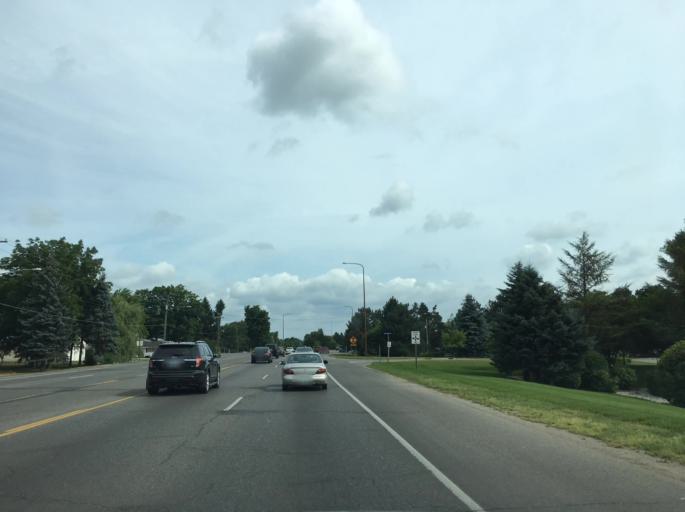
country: US
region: Michigan
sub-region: Grand Traverse County
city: Traverse City
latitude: 44.7285
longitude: -85.6359
